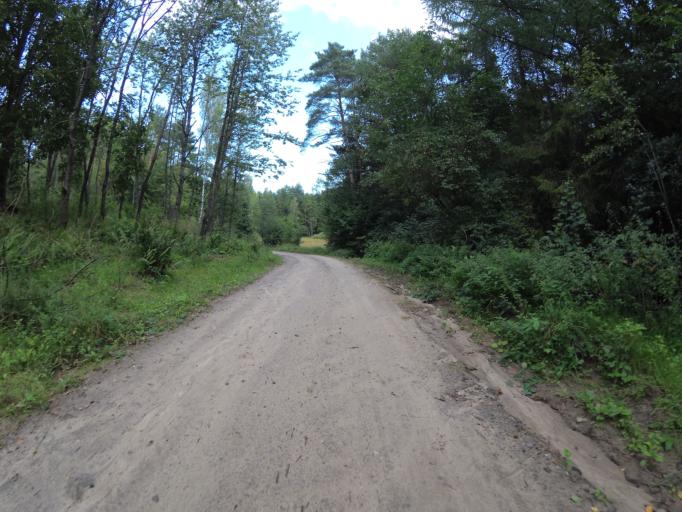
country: PL
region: Pomeranian Voivodeship
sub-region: Gdynia
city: Wielki Kack
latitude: 54.4897
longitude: 18.4677
